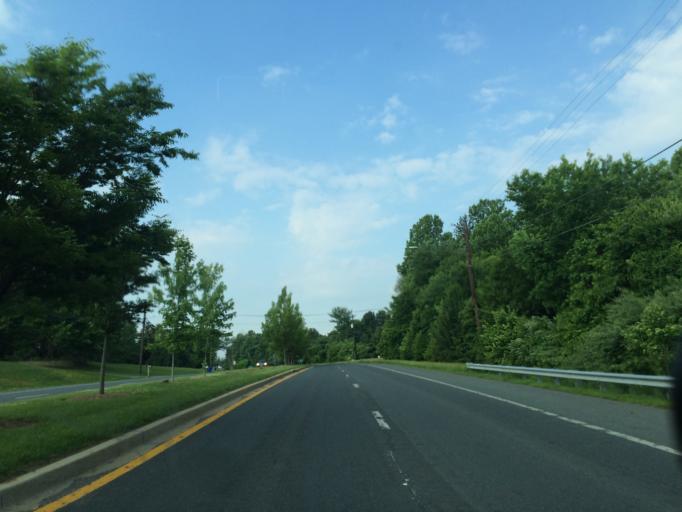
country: US
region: Maryland
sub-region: Montgomery County
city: Cloverly
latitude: 39.1163
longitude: -76.9911
